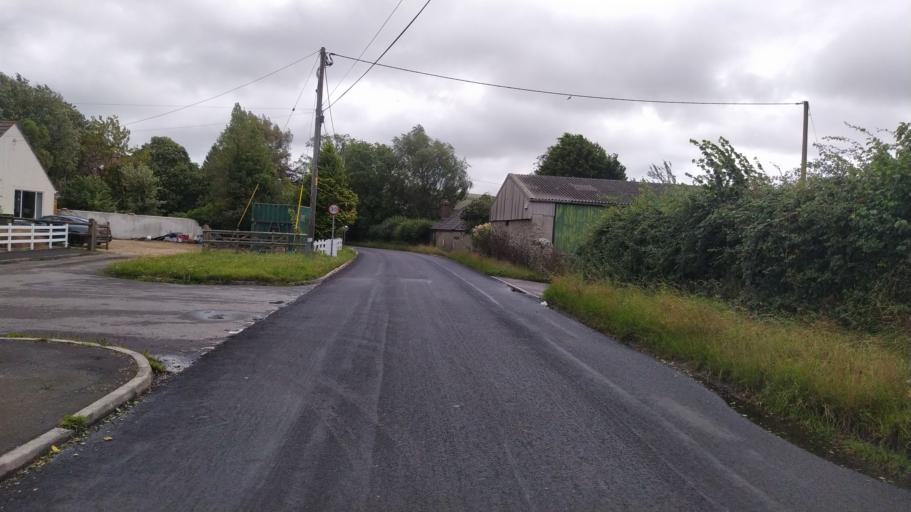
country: GB
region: England
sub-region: Dorset
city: Shaftesbury
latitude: 50.9874
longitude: -2.1667
